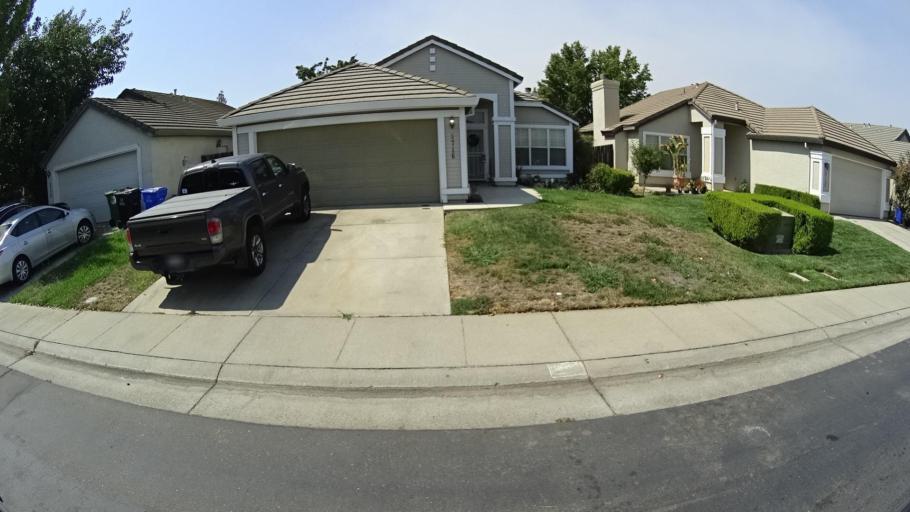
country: US
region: California
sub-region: Sacramento County
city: Elk Grove
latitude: 38.4414
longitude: -121.3742
